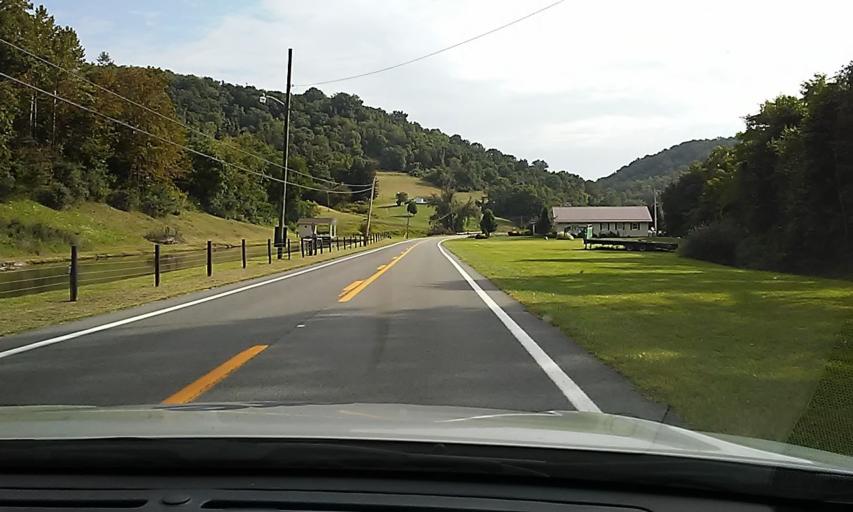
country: US
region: West Virginia
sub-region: Marion County
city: Mannington
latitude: 39.6604
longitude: -80.3799
